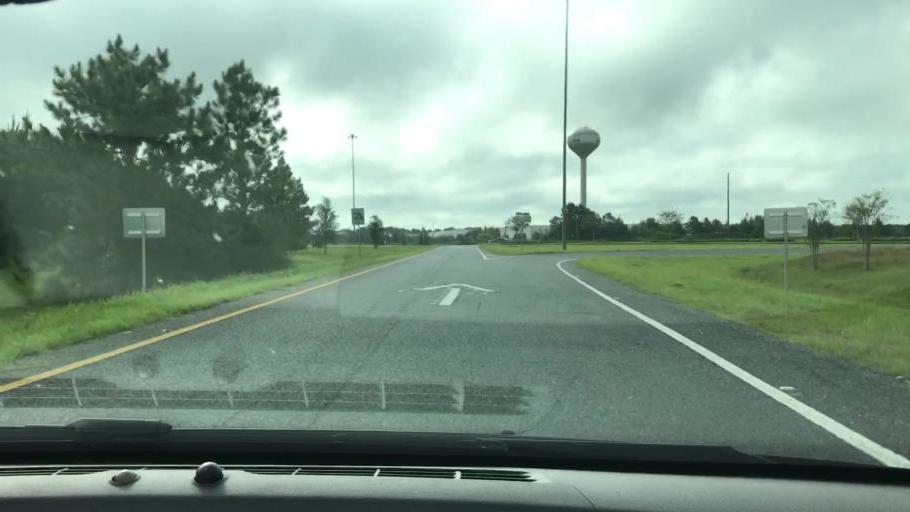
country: US
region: Florida
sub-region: Jackson County
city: Marianna
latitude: 30.7538
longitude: -85.2751
